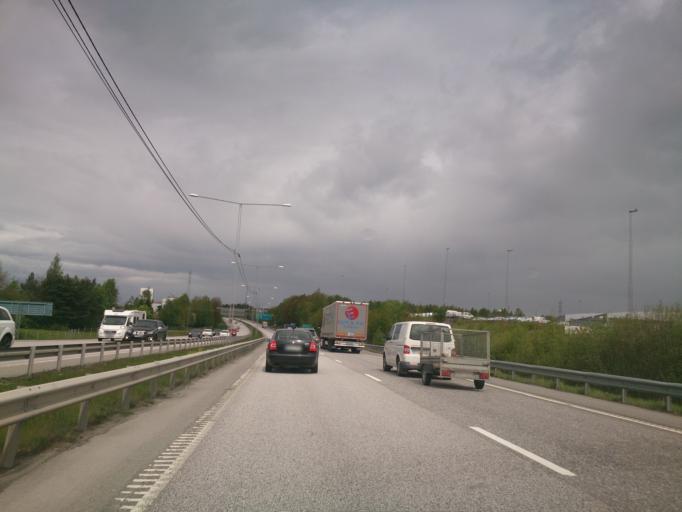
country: SE
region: Stockholm
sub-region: Sodertalje Kommun
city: Pershagen
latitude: 59.1674
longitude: 17.6494
